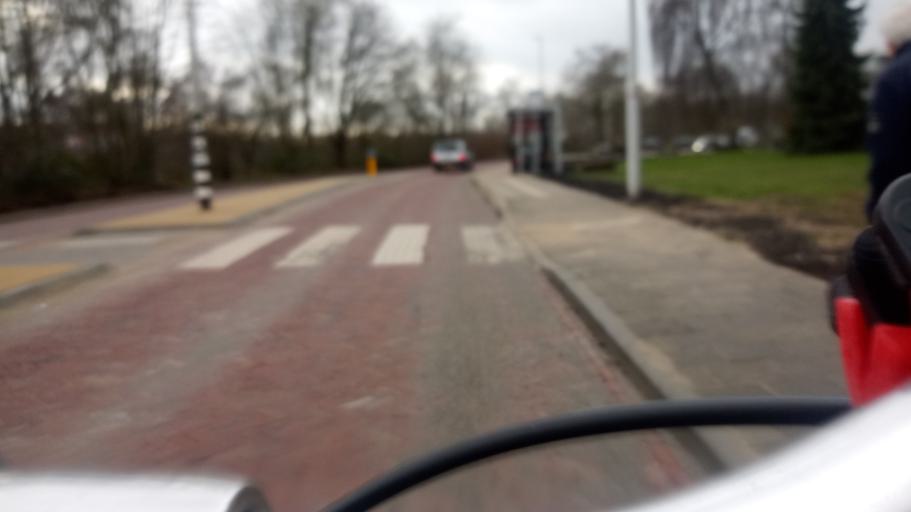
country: NL
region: Gelderland
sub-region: Gemeente Nijmegen
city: Nijmegen
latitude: 51.8072
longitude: 5.8373
